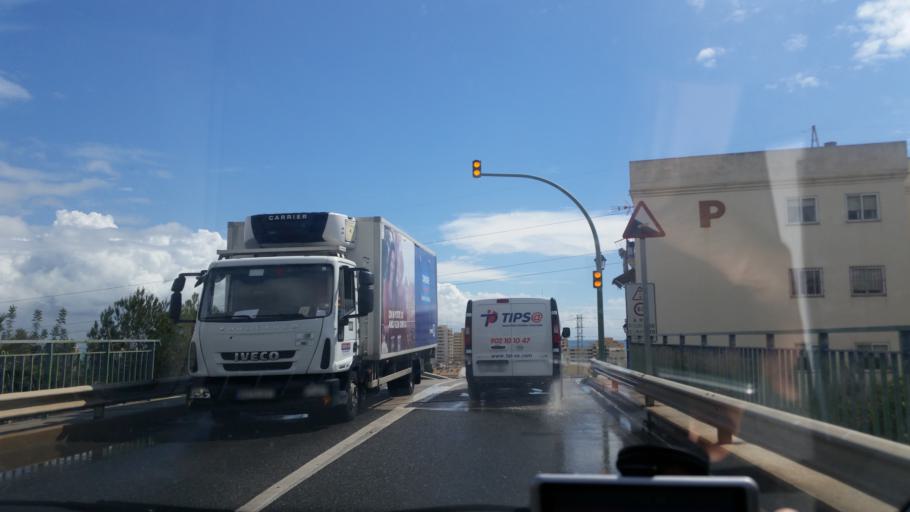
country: ES
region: Andalusia
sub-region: Provincia de Malaga
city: Fuengirola
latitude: 36.5584
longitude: -4.6198
